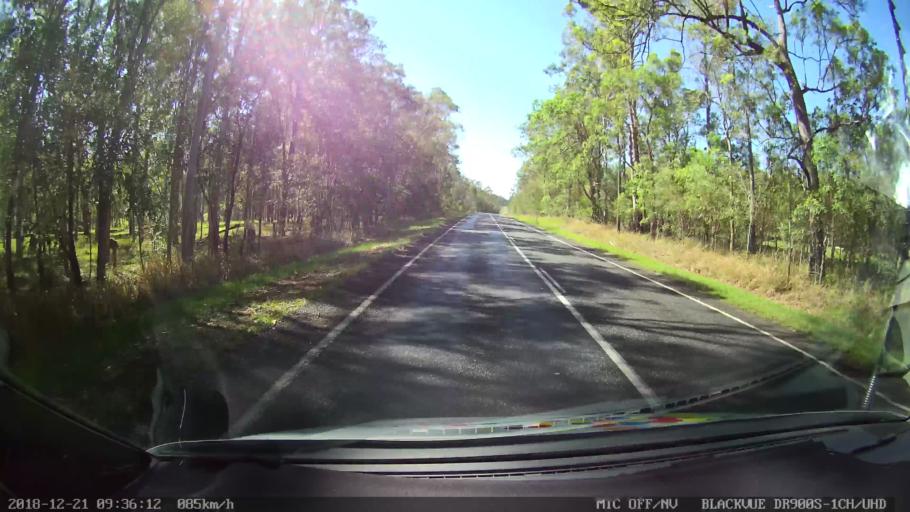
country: AU
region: New South Wales
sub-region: Clarence Valley
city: Grafton
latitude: -29.5204
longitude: 152.9823
